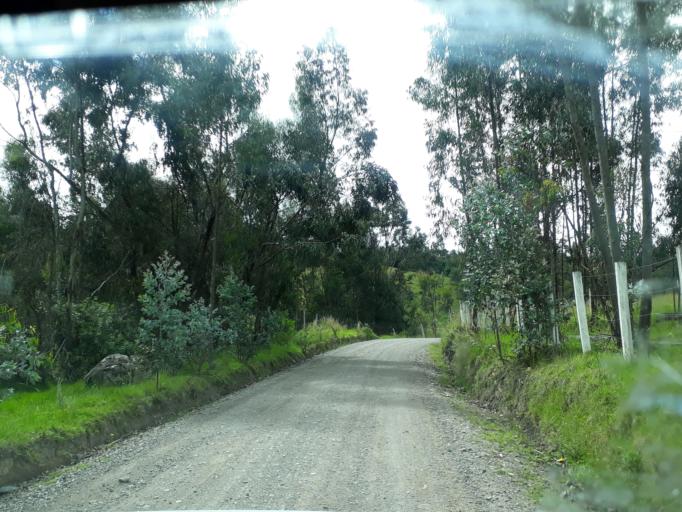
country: CO
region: Cundinamarca
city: La Mesa
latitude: 5.2798
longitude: -73.9077
